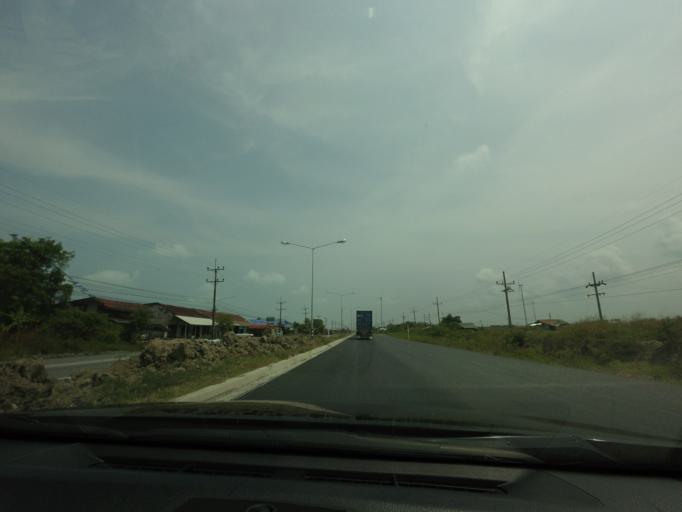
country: TH
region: Nakhon Si Thammarat
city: Hua Sai
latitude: 7.9243
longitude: 100.3350
